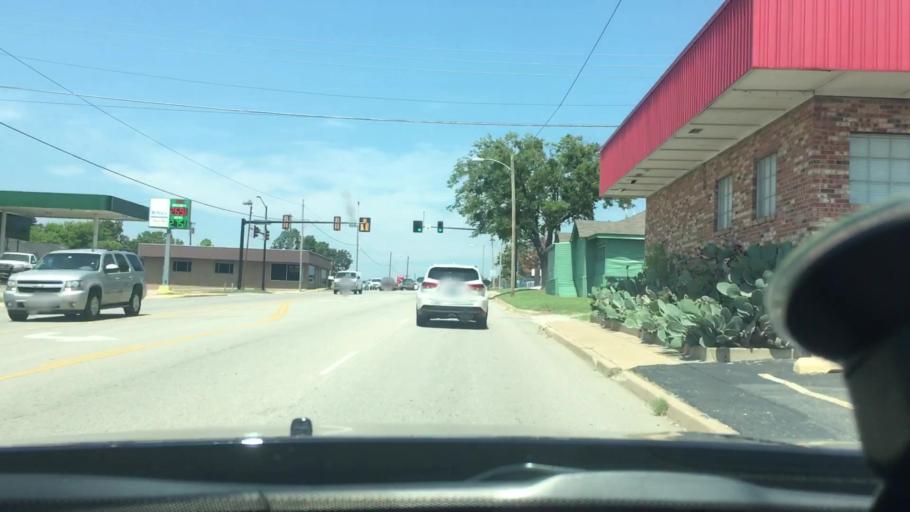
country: US
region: Oklahoma
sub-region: Pontotoc County
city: Ada
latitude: 34.7684
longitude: -96.6698
